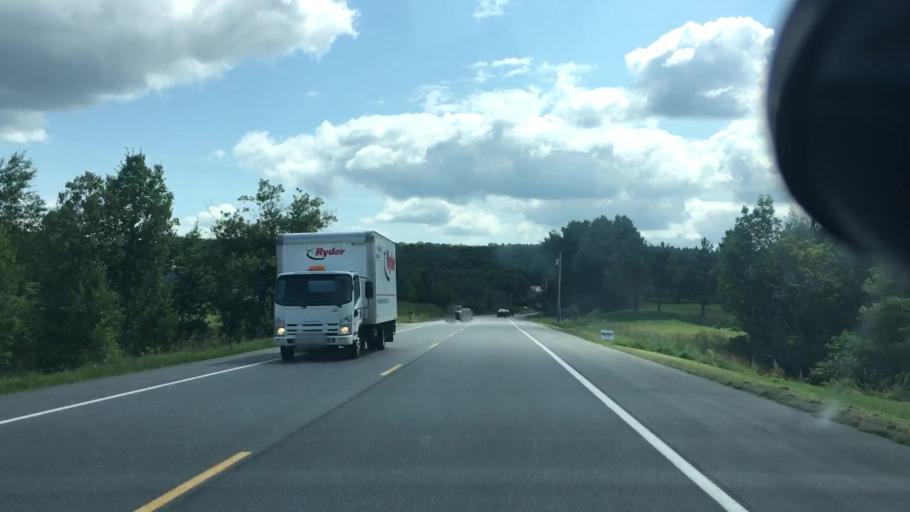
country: US
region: Maine
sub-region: Kennebec County
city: Waterville
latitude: 44.6024
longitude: -69.6585
